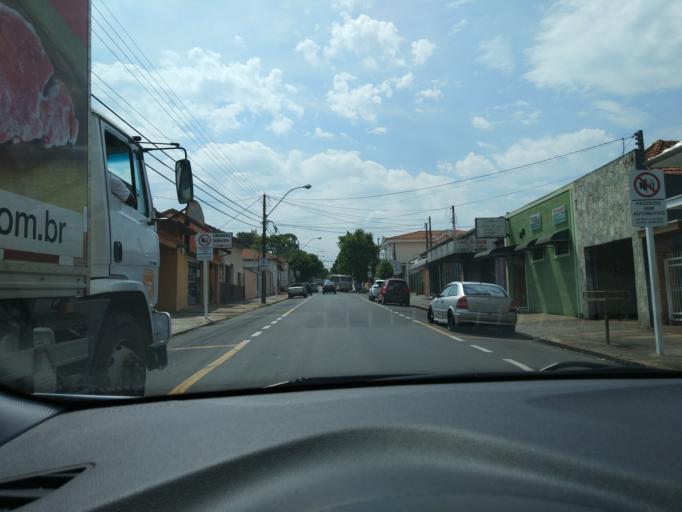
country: BR
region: Sao Paulo
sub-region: Botucatu
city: Botucatu
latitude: -22.8729
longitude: -48.4455
